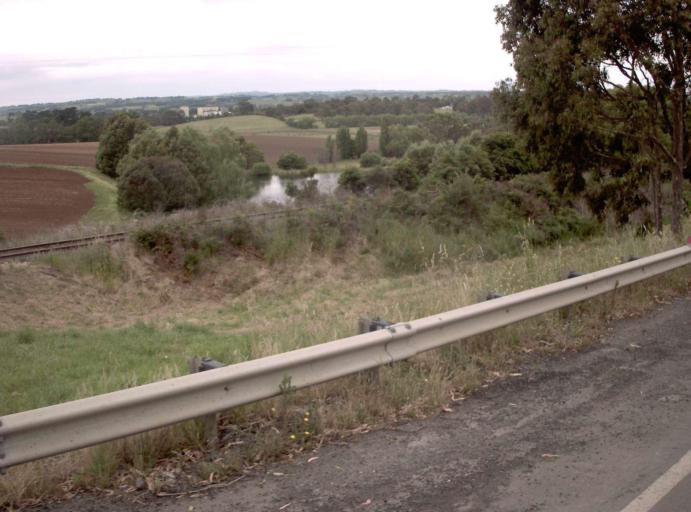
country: AU
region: Victoria
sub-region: Baw Baw
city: Warragul
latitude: -38.4615
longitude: 145.9334
